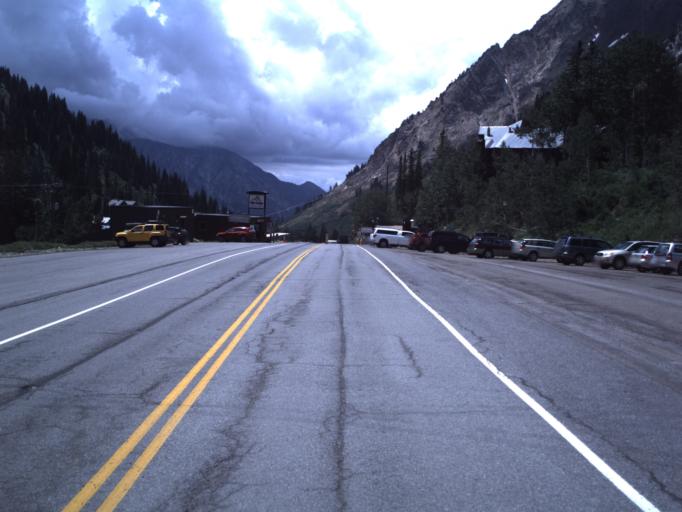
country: US
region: Utah
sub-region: Summit County
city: Snyderville
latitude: 40.5905
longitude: -111.6356
